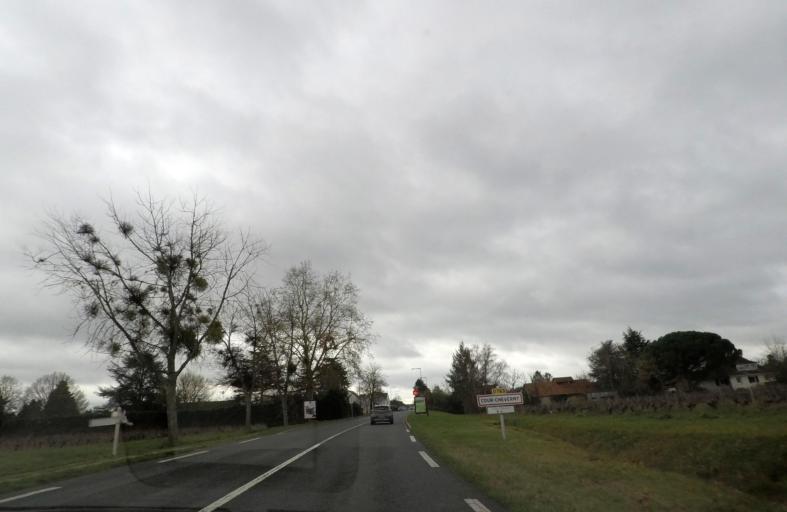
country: FR
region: Centre
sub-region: Departement du Loir-et-Cher
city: Cour-Cheverny
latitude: 47.5156
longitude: 1.4530
